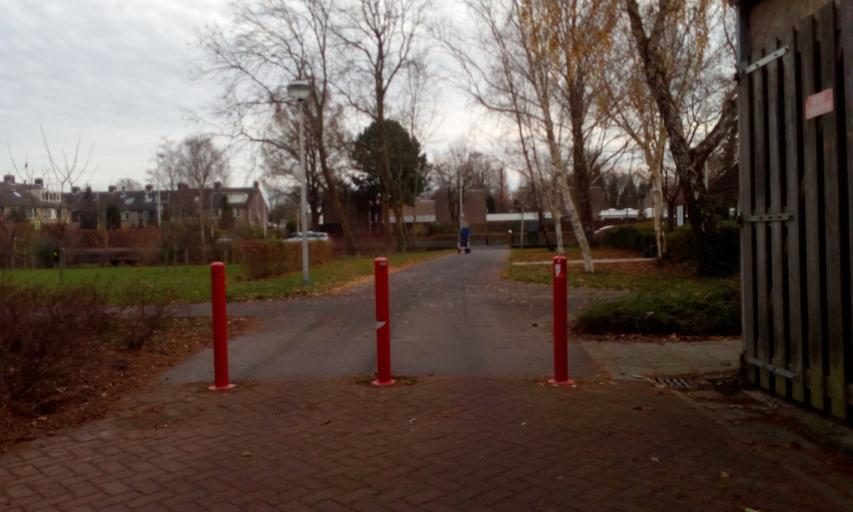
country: NL
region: South Holland
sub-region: Gemeente Lansingerland
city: Berkel en Rodenrijs
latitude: 51.9988
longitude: 4.4870
